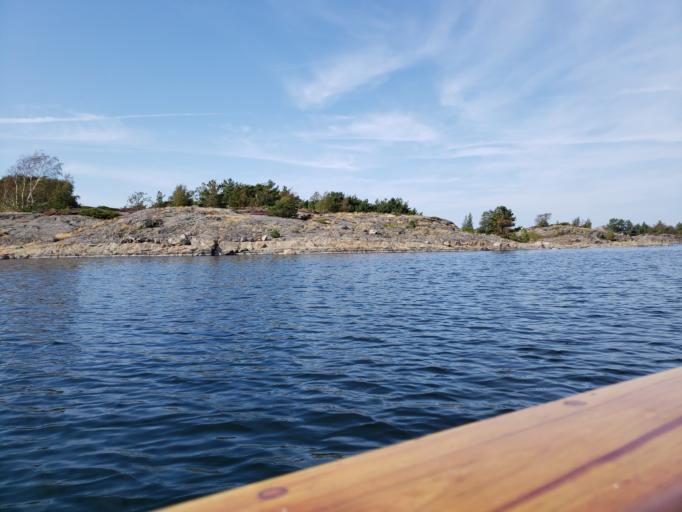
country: FI
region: Varsinais-Suomi
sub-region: Aboland-Turunmaa
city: Dragsfjaerd
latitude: 59.8483
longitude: 22.2085
